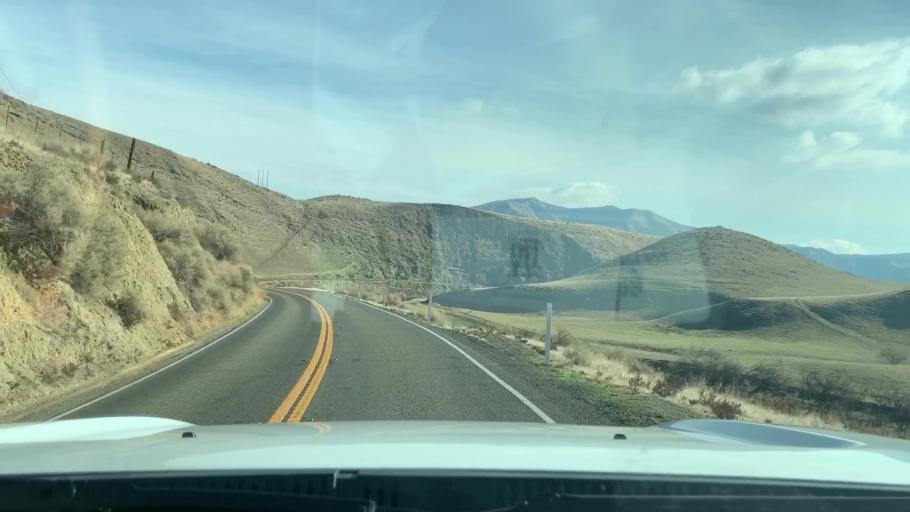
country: US
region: California
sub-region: Fresno County
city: Coalinga
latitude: 36.0938
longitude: -120.4338
